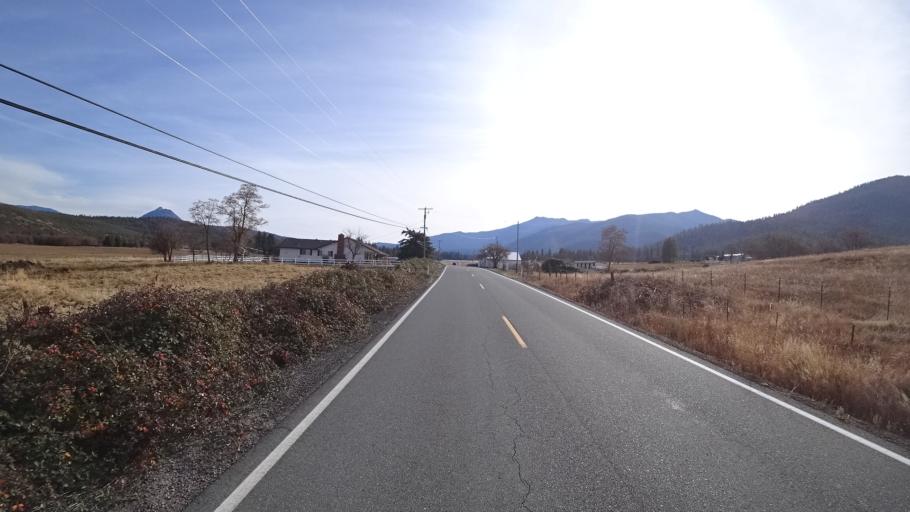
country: US
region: California
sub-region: Siskiyou County
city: Weed
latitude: 41.4251
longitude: -122.4370
